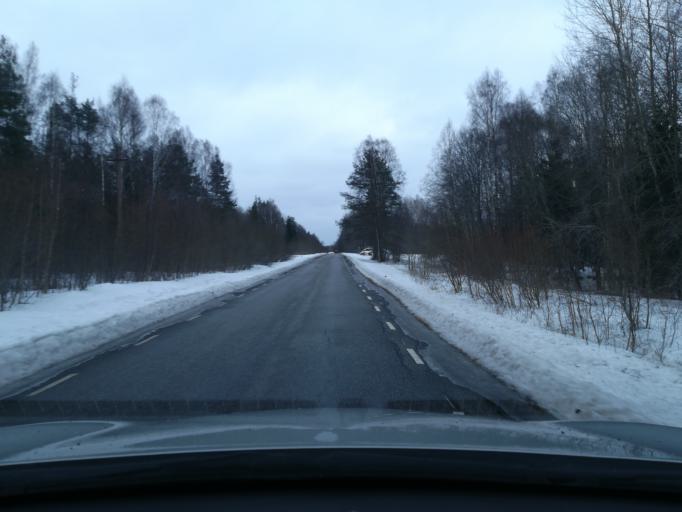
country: EE
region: Harju
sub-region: Nissi vald
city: Turba
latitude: 59.0663
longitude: 24.2524
